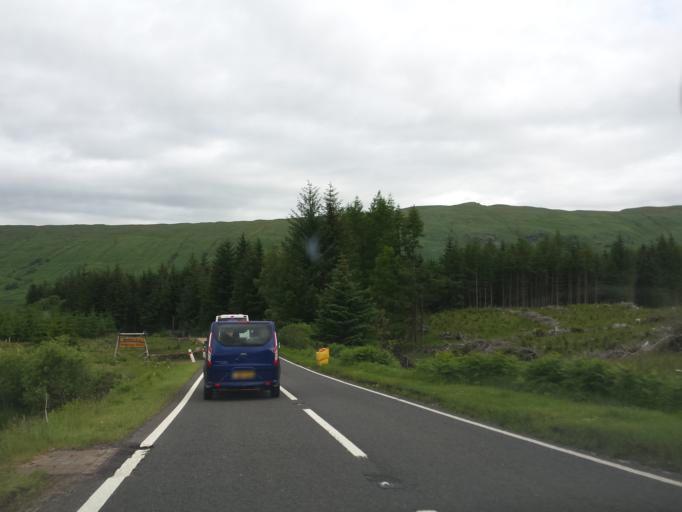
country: GB
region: Scotland
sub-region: Stirling
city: Callander
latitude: 56.4387
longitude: -4.3522
